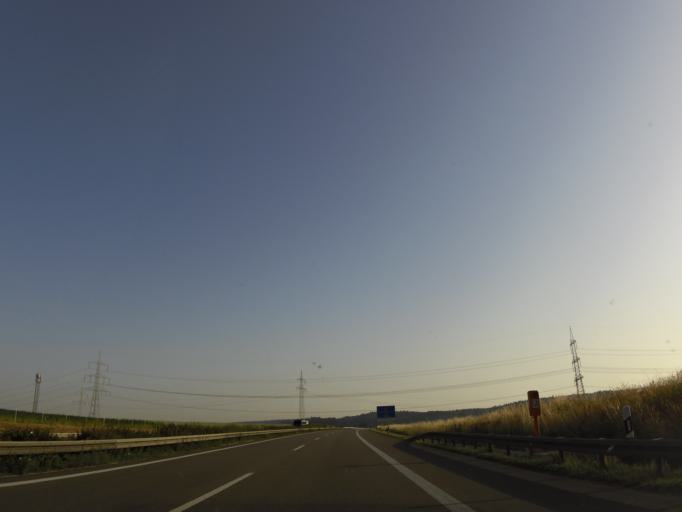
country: DE
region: Bavaria
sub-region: Swabia
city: Bellenberg
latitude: 48.2553
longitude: 10.1137
